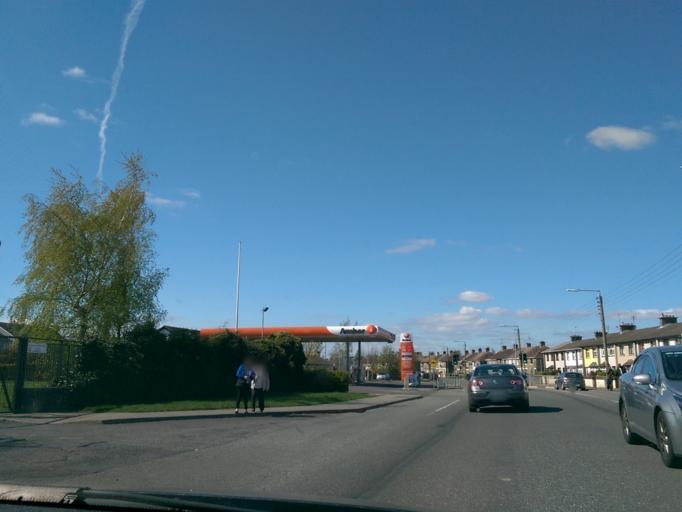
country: IE
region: Leinster
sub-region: Kildare
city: Athy
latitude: 52.9946
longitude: -6.9906
